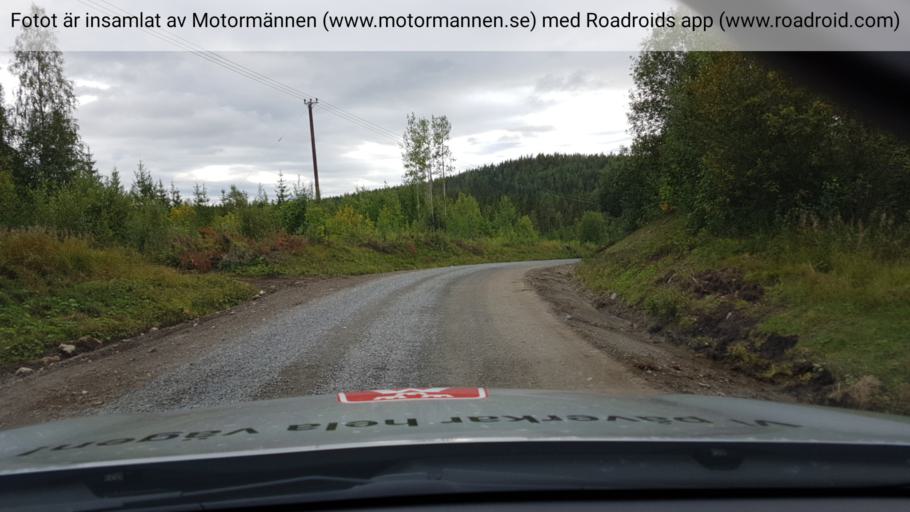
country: SE
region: Jaemtland
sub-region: Ragunda Kommun
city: Hammarstrand
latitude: 62.9003
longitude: 16.0916
